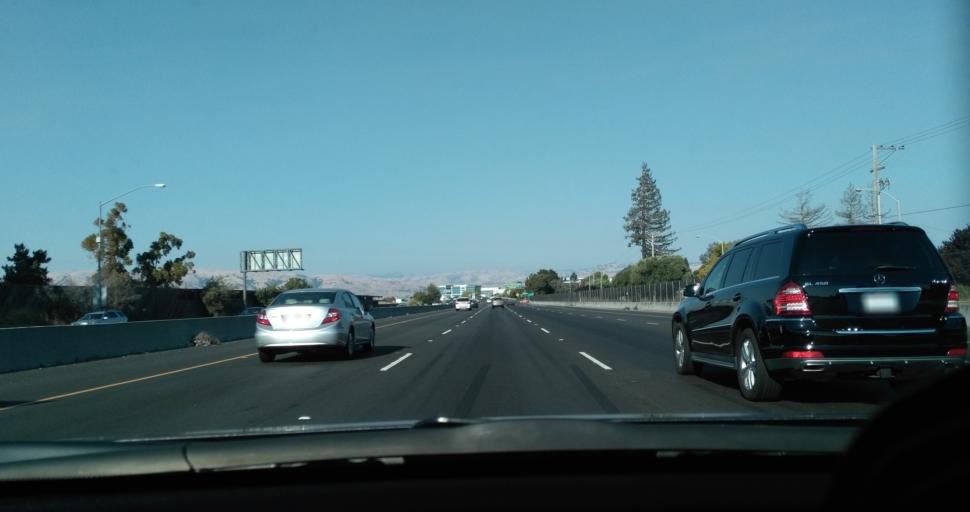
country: US
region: California
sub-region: Santa Clara County
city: Sunnyvale
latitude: 37.4101
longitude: -121.9945
